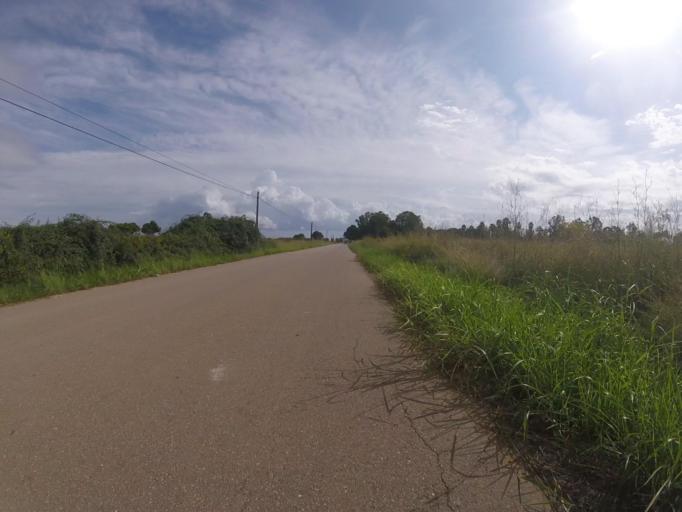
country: ES
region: Valencia
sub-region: Provincia de Castello
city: Orpesa/Oropesa del Mar
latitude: 40.1313
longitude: 0.1599
